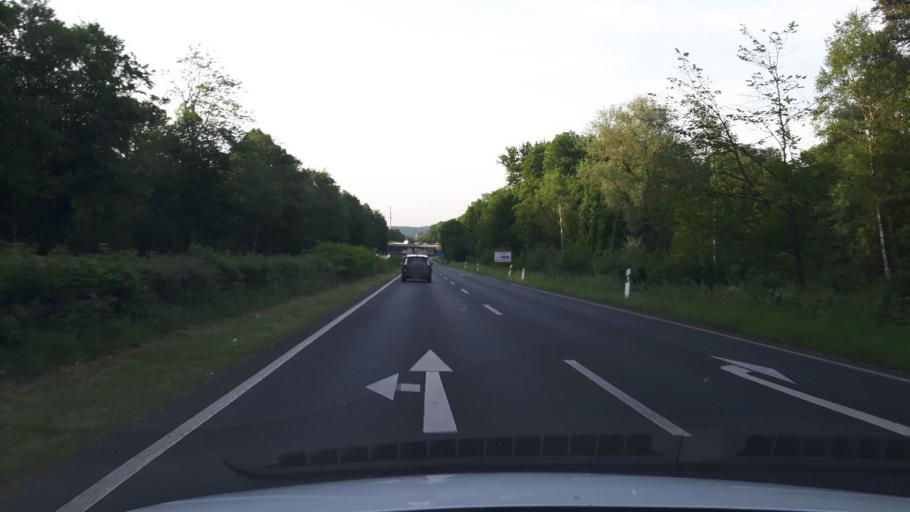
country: DE
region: North Rhine-Westphalia
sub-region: Regierungsbezirk Koln
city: Siegburg
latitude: 50.8184
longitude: 7.2053
